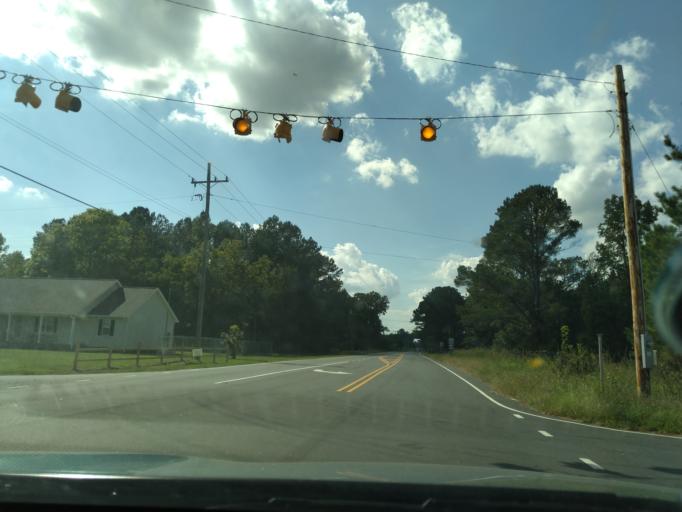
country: US
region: North Carolina
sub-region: Martin County
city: Robersonville
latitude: 35.8232
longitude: -77.3108
